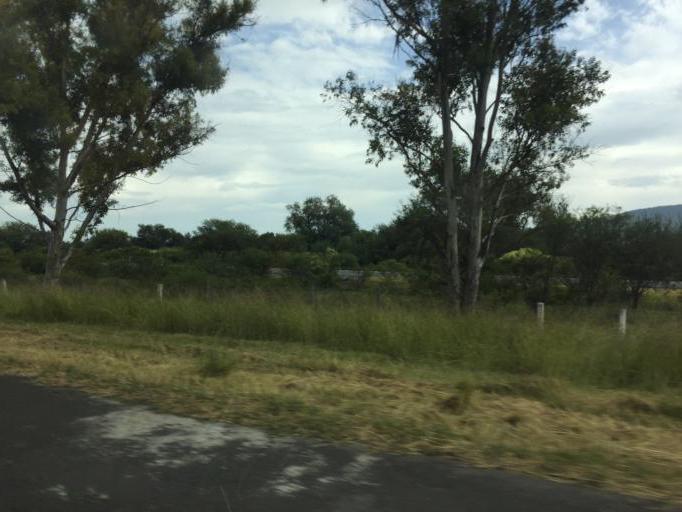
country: MX
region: Jalisco
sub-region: Ocotlan
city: Joconoxtle (La Tuna)
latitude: 20.3777
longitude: -102.6816
